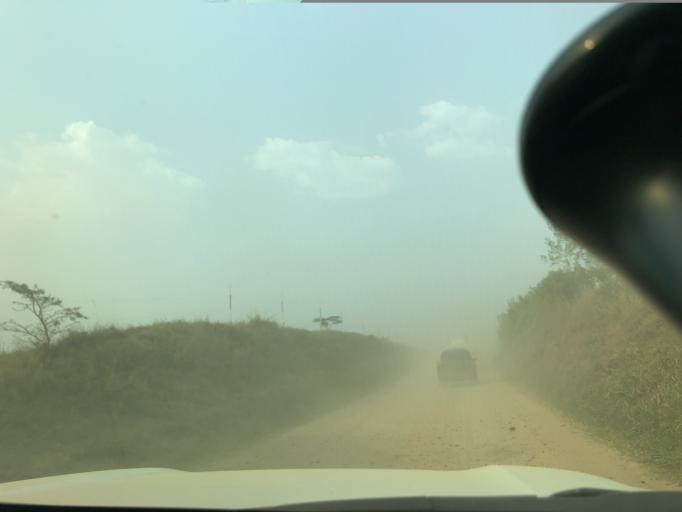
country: CD
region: Nord Kivu
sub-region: North Kivu
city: Butembo
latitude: 0.1127
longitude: 29.6395
